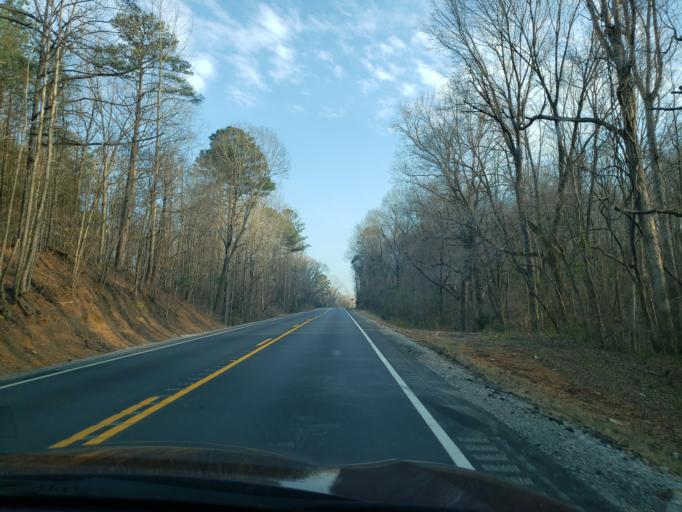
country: US
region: Alabama
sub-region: Hale County
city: Greensboro
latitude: 32.8129
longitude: -87.5963
